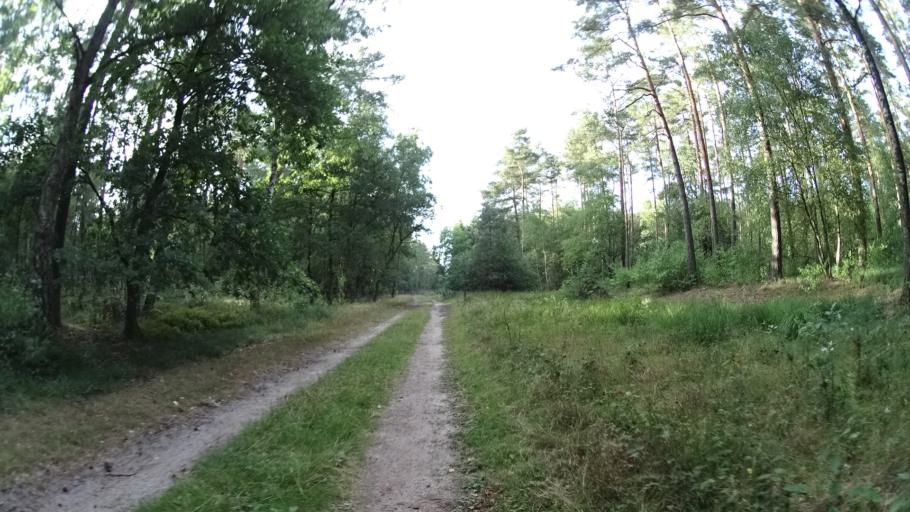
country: DE
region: Lower Saxony
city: Handeloh
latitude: 53.2245
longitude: 9.8754
